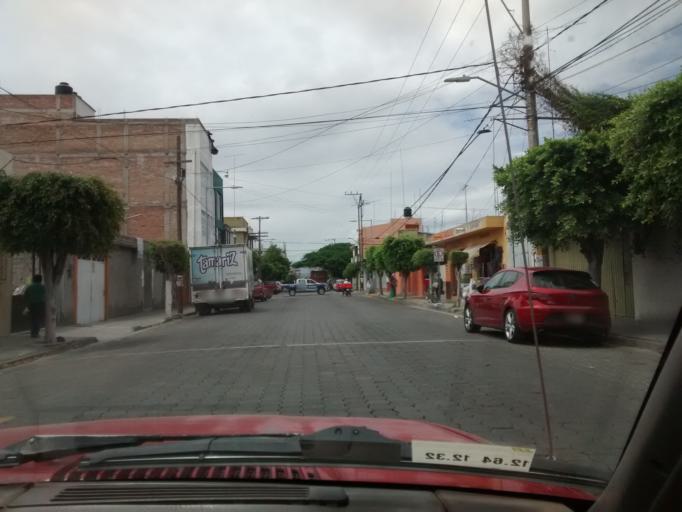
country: MX
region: Puebla
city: Tehuacan
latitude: 18.4656
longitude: -97.3980
